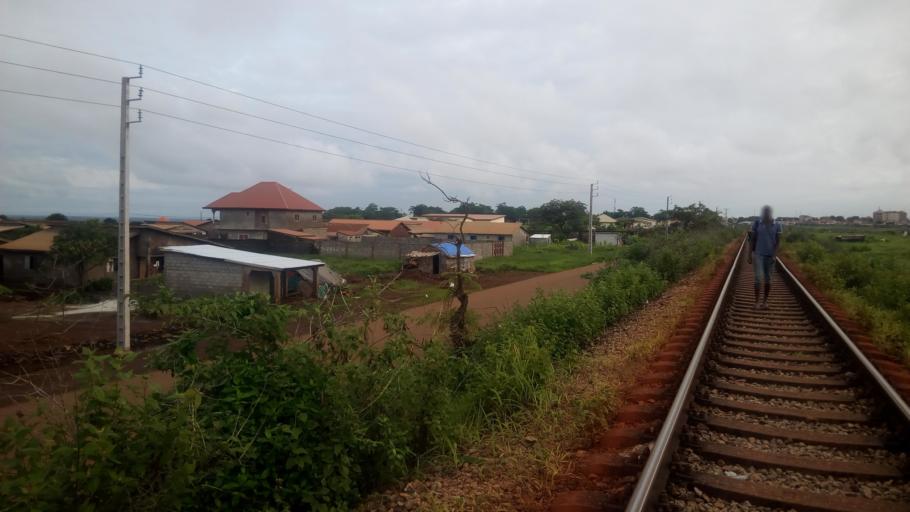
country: GN
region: Kindia
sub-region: Prefecture de Dubreka
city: Dubreka
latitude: 9.7206
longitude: -13.4932
